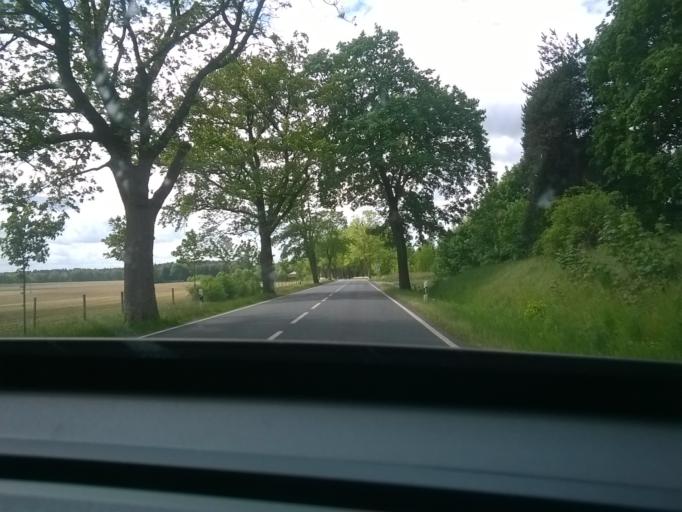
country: DE
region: Brandenburg
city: Wittstock
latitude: 53.1298
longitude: 12.4885
